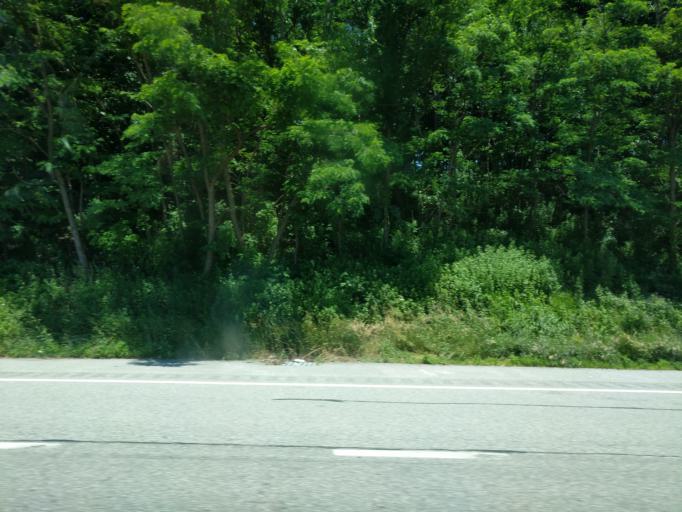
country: US
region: New York
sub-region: Orange County
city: Harriman
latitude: 41.3212
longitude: -74.1495
